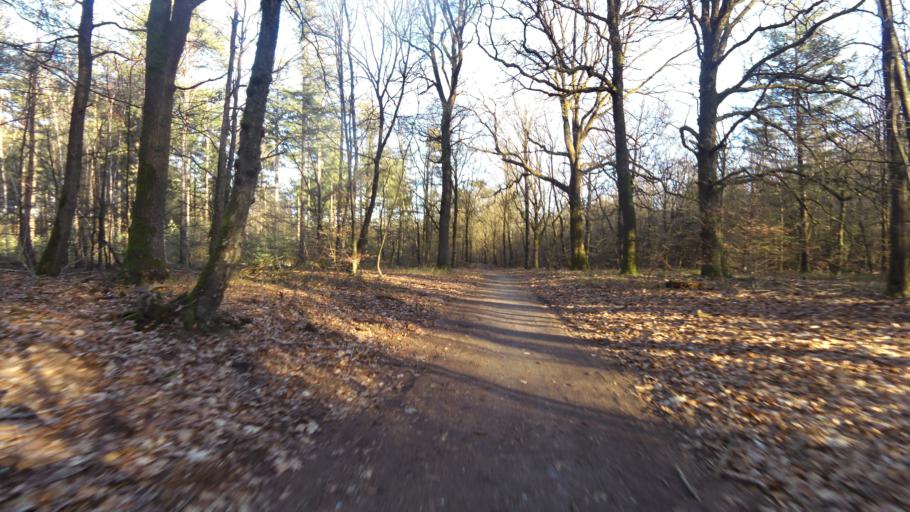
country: NL
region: Gelderland
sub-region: Gemeente Ermelo
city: Ermelo
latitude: 52.2700
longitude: 5.6466
